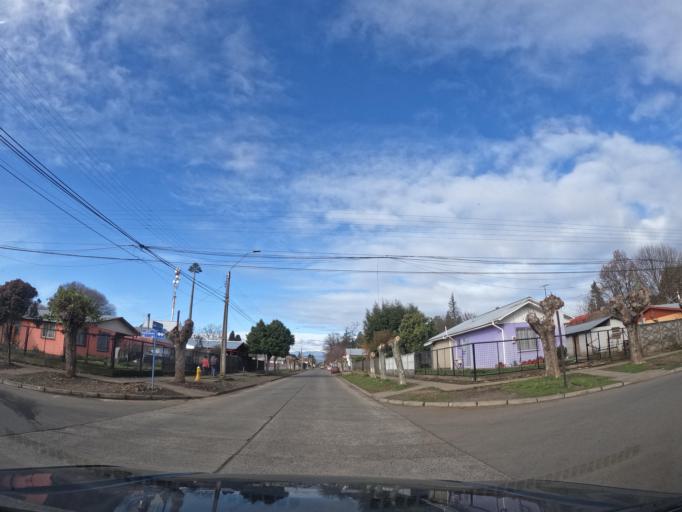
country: CL
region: Biobio
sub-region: Provincia de Nuble
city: Coihueco
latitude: -36.7025
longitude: -71.8944
